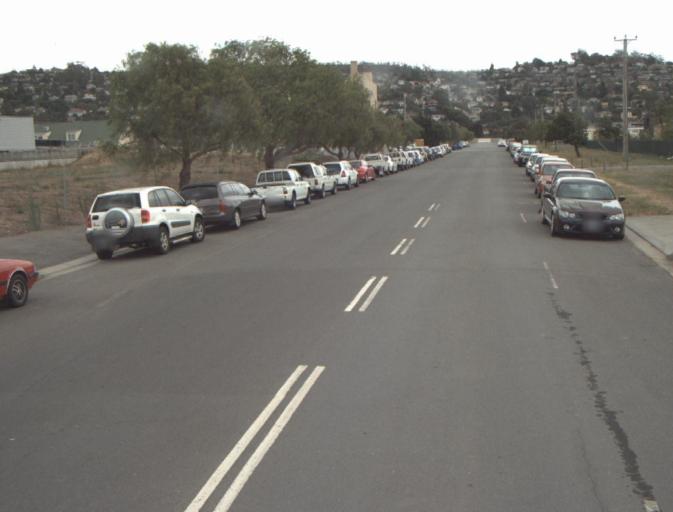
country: AU
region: Tasmania
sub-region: Launceston
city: Launceston
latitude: -41.4307
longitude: 147.1326
